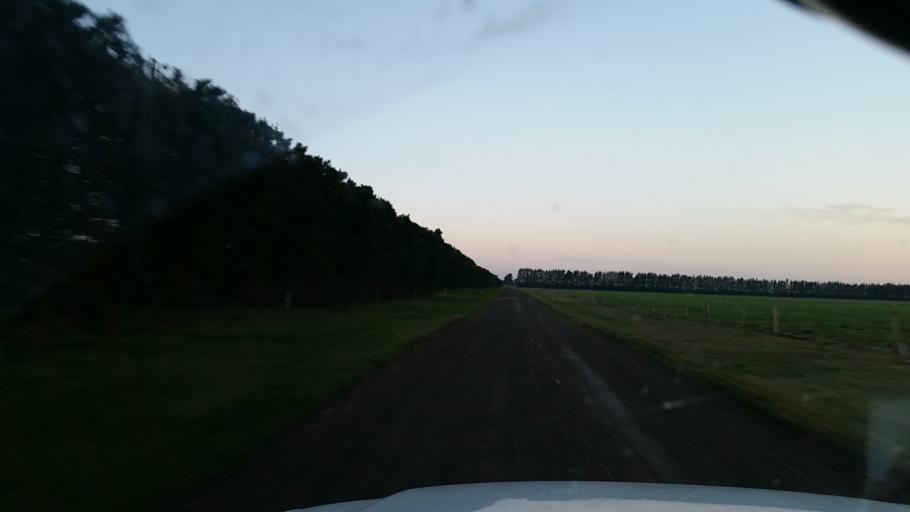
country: NZ
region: Canterbury
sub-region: Ashburton District
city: Tinwald
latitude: -43.9474
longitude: 171.6020
